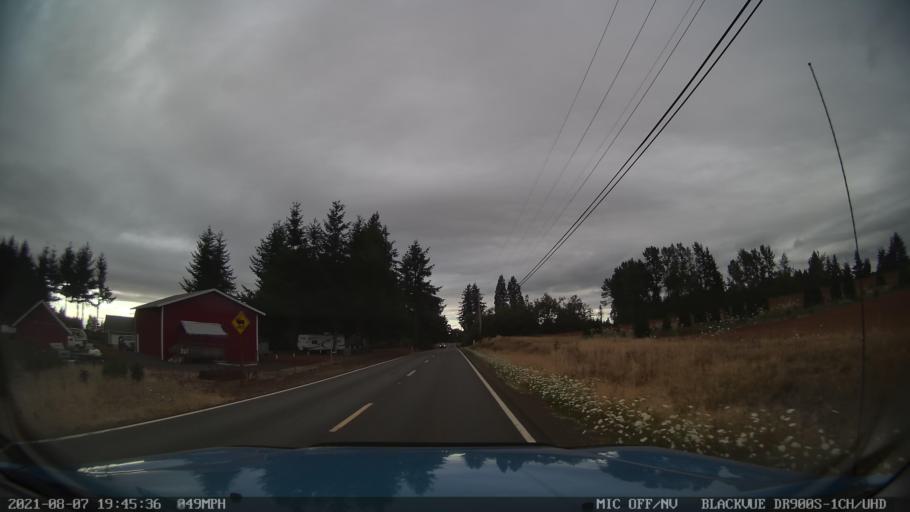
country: US
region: Oregon
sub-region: Marion County
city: Silverton
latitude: 44.9498
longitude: -122.6971
